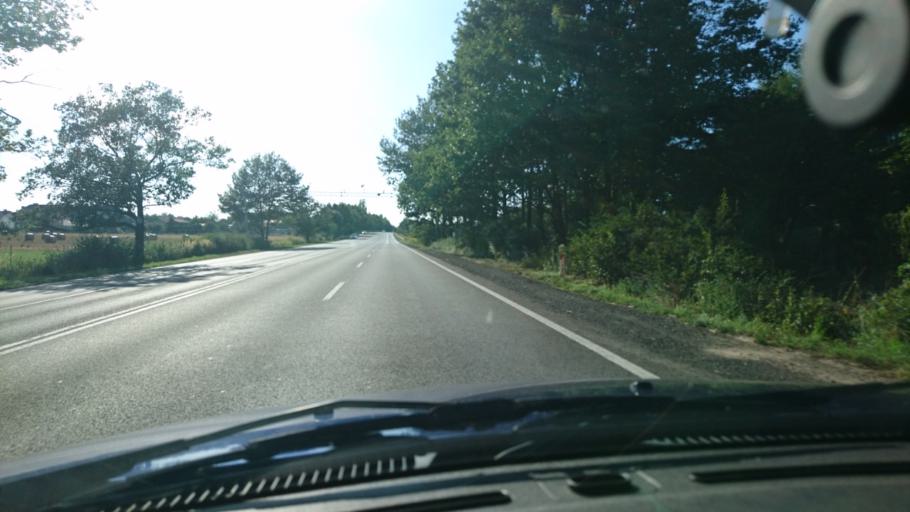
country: PL
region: Silesian Voivodeship
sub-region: Gliwice
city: Gliwice
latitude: 50.3131
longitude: 18.7064
